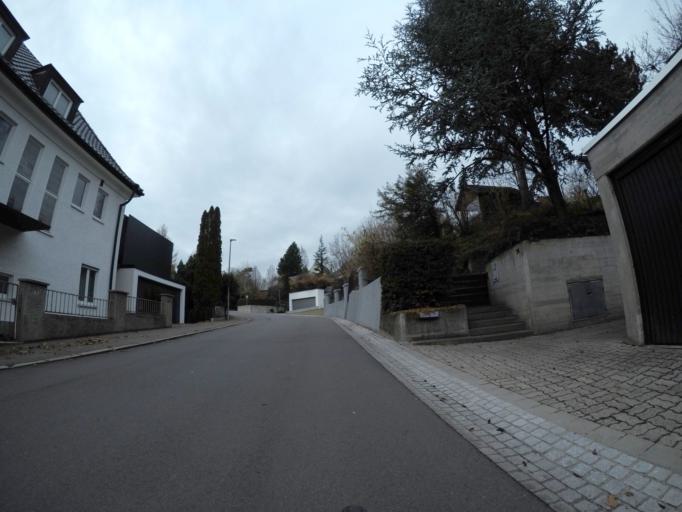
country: DE
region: Baden-Wuerttemberg
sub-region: Tuebingen Region
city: Reutlingen
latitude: 48.4974
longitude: 9.2247
